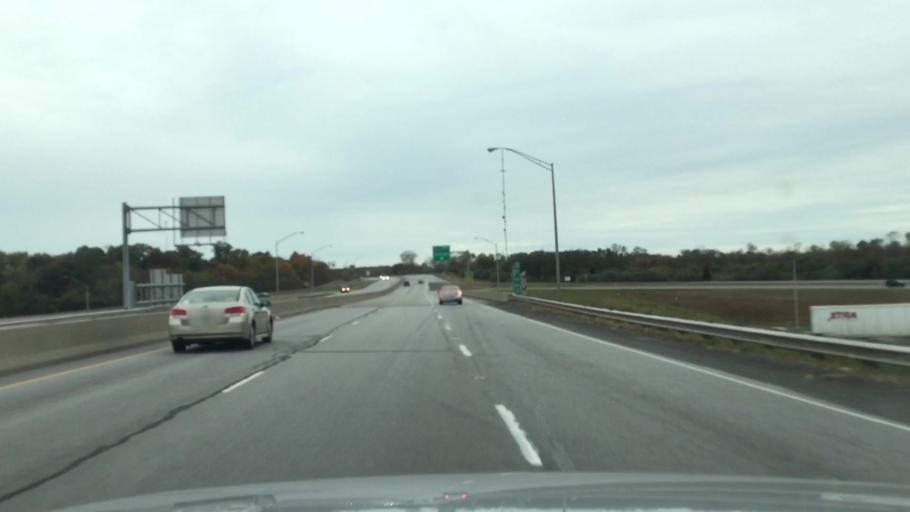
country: US
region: Indiana
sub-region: Porter County
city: Chesterton
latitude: 41.6237
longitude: -87.0451
